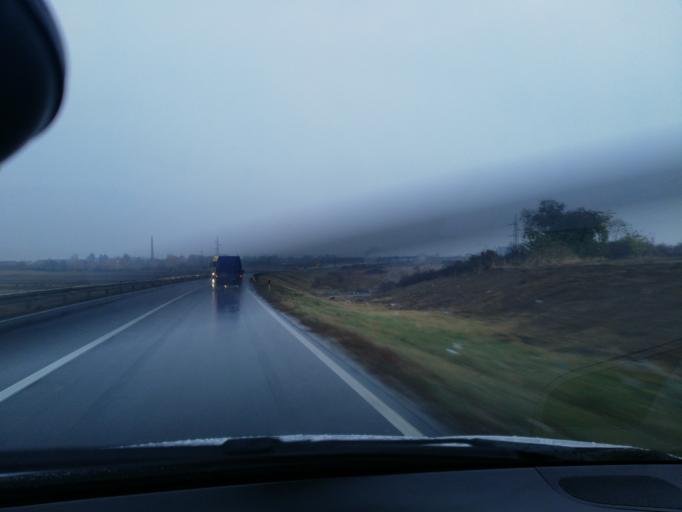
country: RS
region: Autonomna Pokrajina Vojvodina
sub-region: Sremski Okrug
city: Ruma
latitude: 45.0143
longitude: 19.8450
